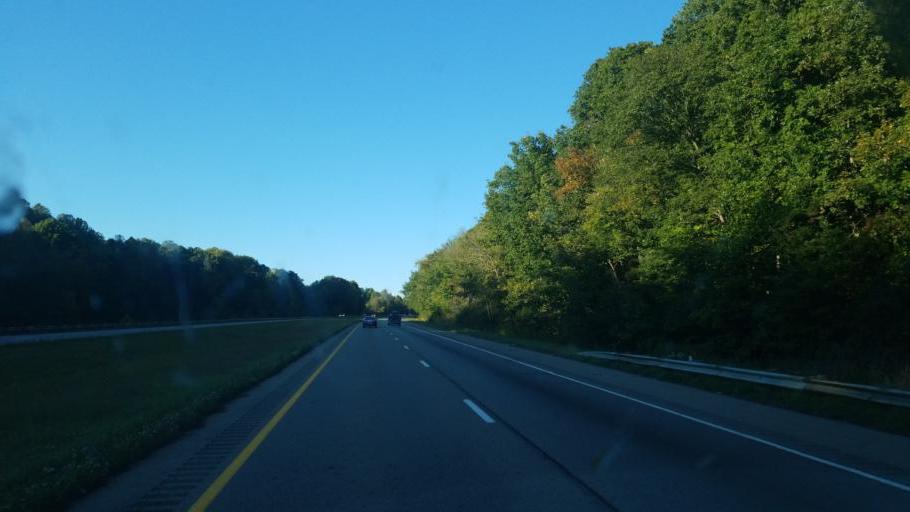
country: US
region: Ohio
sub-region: Tuscarawas County
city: Newcomerstown
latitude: 40.2006
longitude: -81.5569
